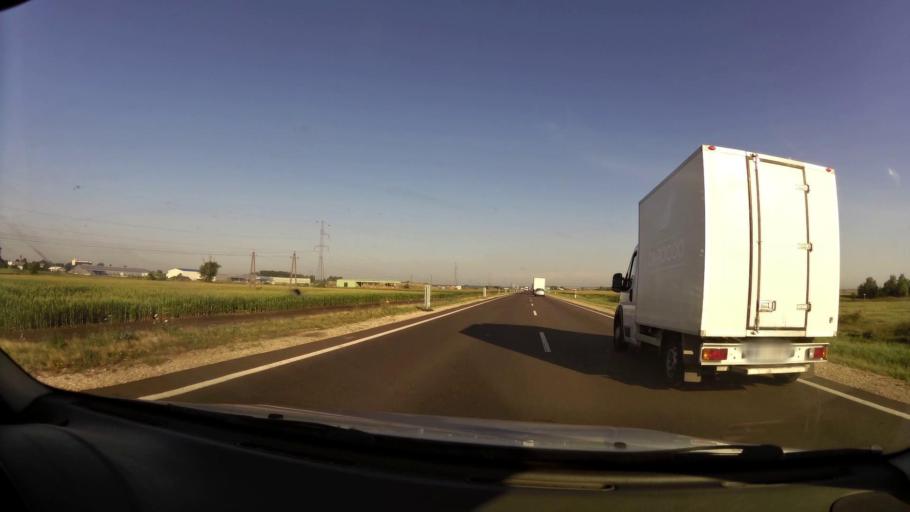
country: HU
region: Pest
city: Cegled
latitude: 47.1995
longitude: 19.7955
